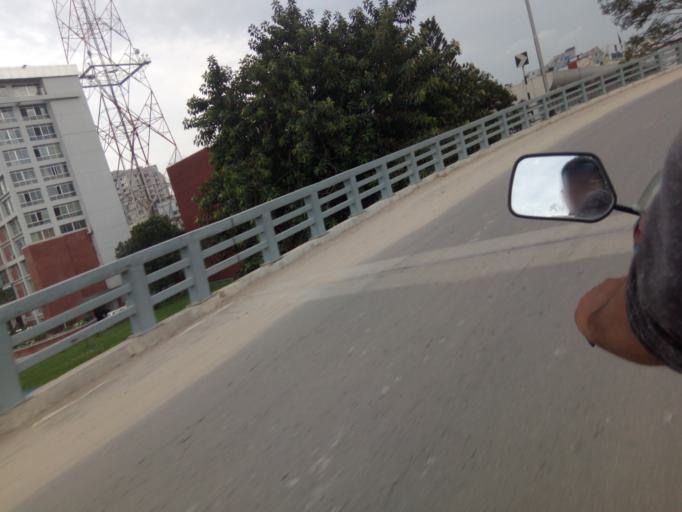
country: BD
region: Dhaka
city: Paltan
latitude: 23.7665
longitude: 90.4226
